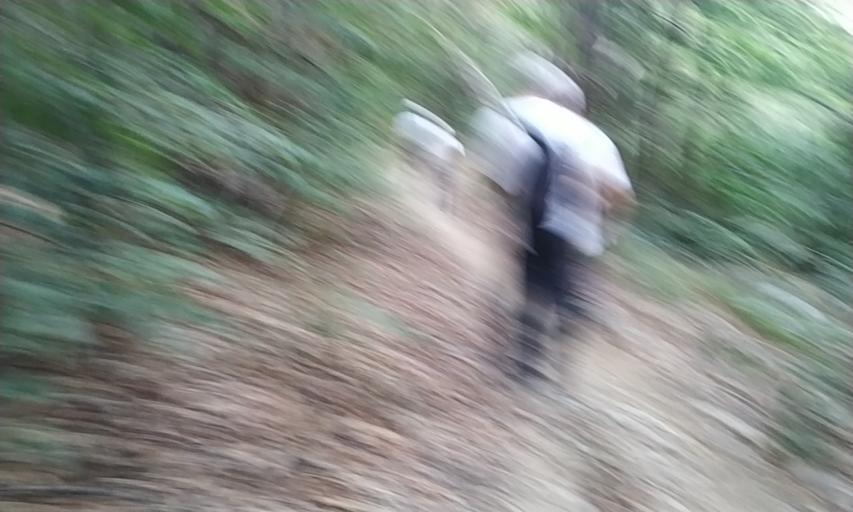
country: IT
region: Piedmont
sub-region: Provincia di Biella
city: Dorzano
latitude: 45.4355
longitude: 8.0829
